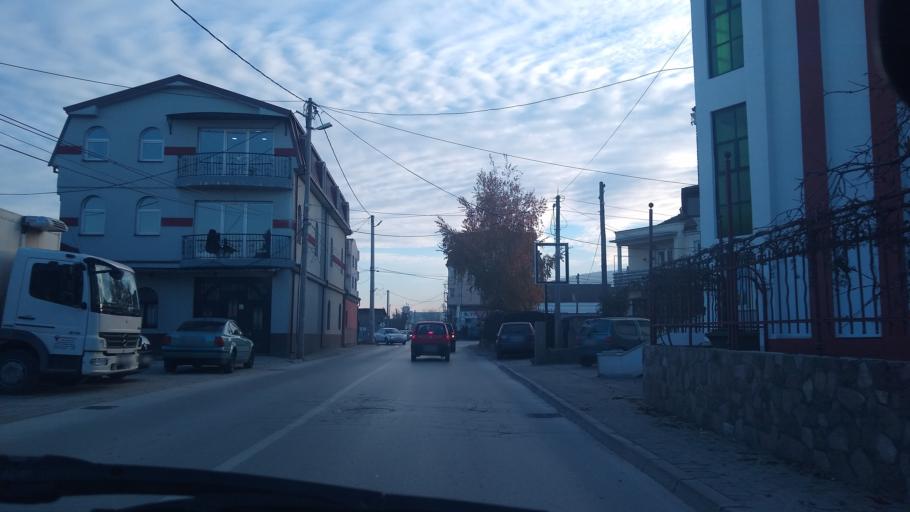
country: MK
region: Bitola
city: Bitola
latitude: 41.0258
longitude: 21.3425
